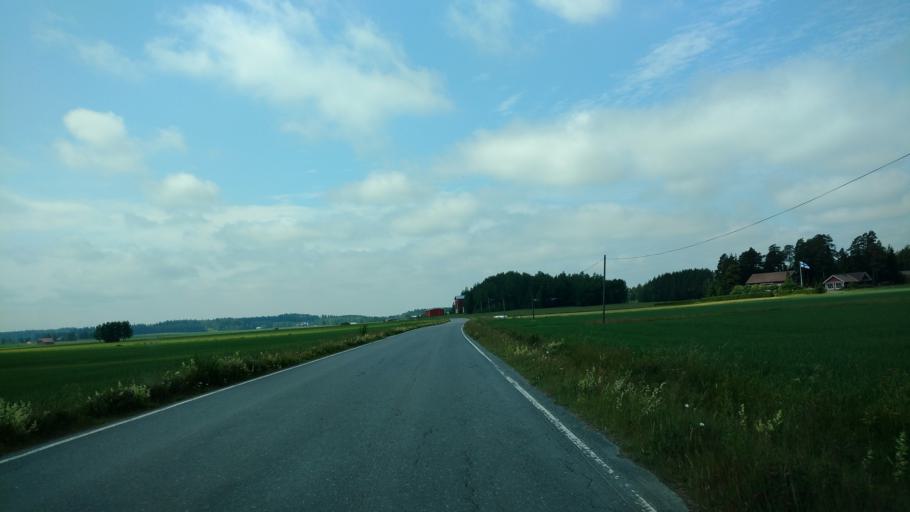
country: FI
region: Haeme
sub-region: Forssa
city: Jokioinen
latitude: 60.7902
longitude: 23.4012
